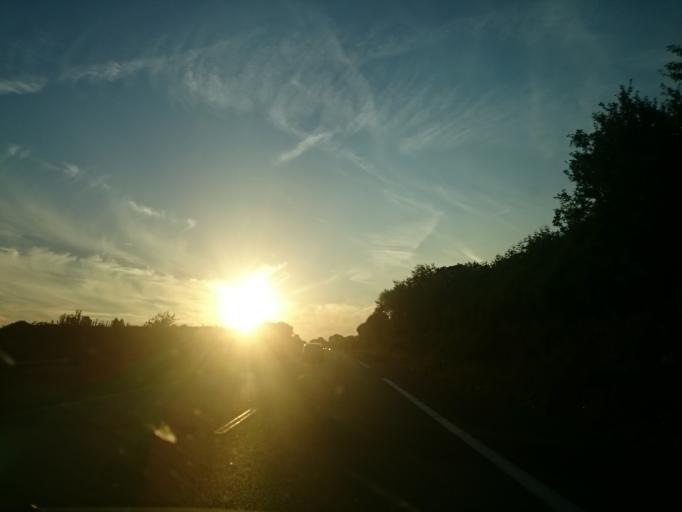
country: FR
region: Brittany
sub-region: Departement du Finistere
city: Le Trevoux
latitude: 47.8755
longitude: -3.6177
